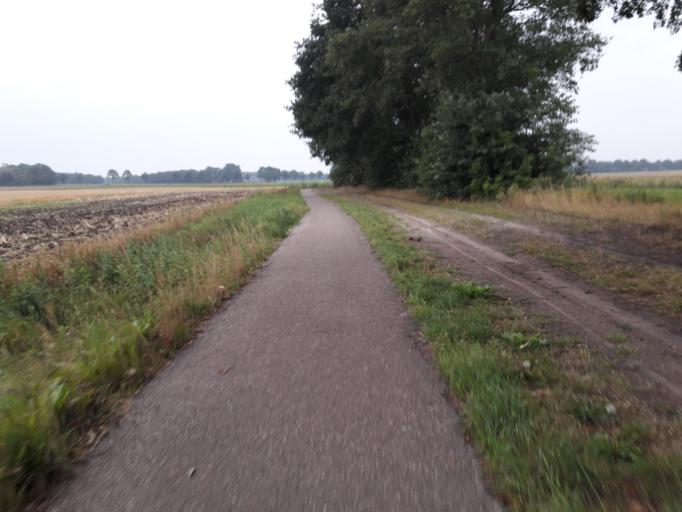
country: NL
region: Drenthe
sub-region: Gemeente Borger-Odoorn
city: Borger
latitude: 52.9328
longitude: 6.8166
